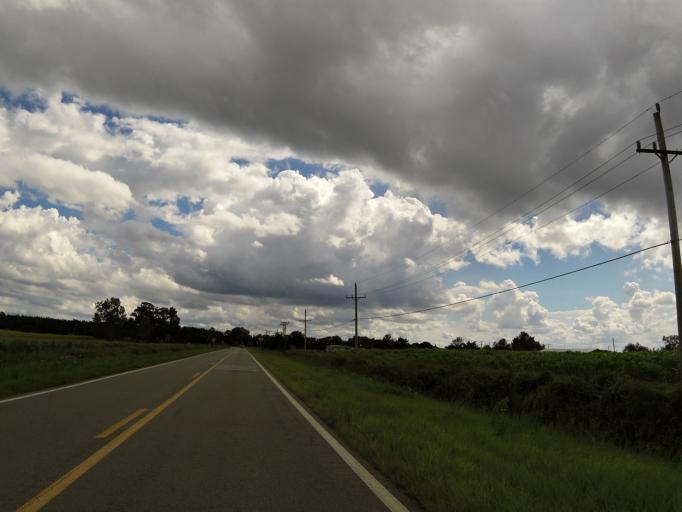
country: US
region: Florida
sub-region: Saint Johns County
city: Saint Augustine South
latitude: 29.8538
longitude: -81.4941
